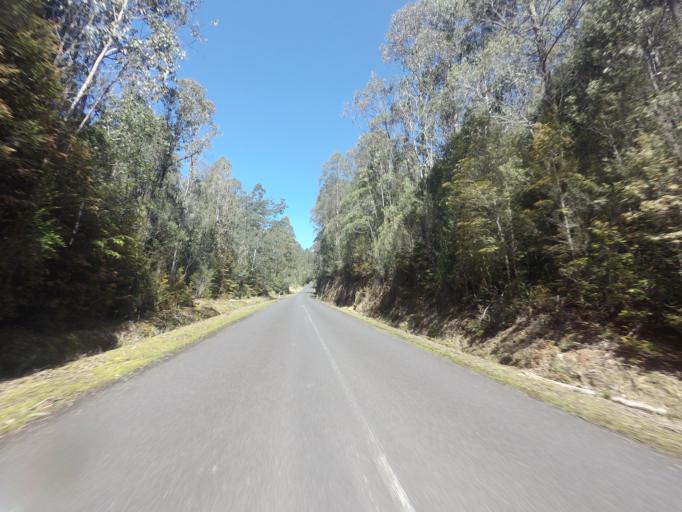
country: AU
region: Tasmania
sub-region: Huon Valley
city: Geeveston
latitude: -42.8225
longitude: 146.3128
